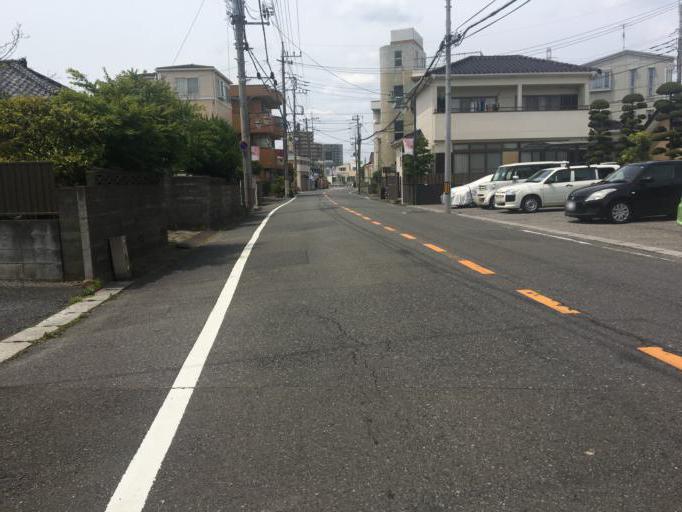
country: JP
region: Saitama
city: Shimotoda
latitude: 35.8365
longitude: 139.6623
